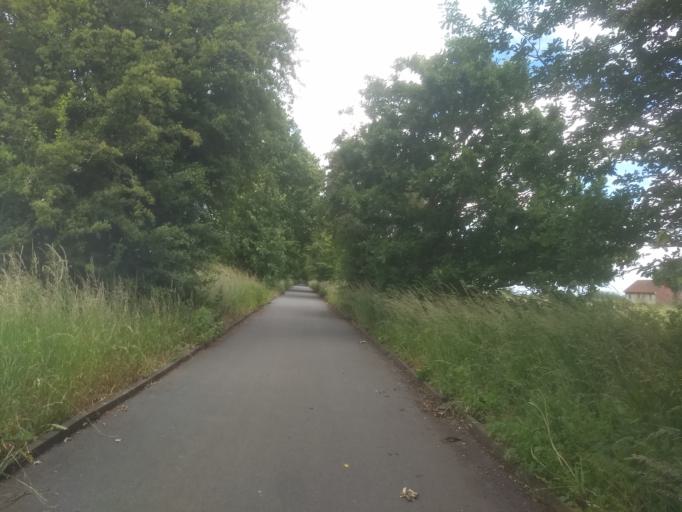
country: FR
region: Nord-Pas-de-Calais
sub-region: Departement du Pas-de-Calais
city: Beaumetz-les-Loges
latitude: 50.2348
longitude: 2.6498
